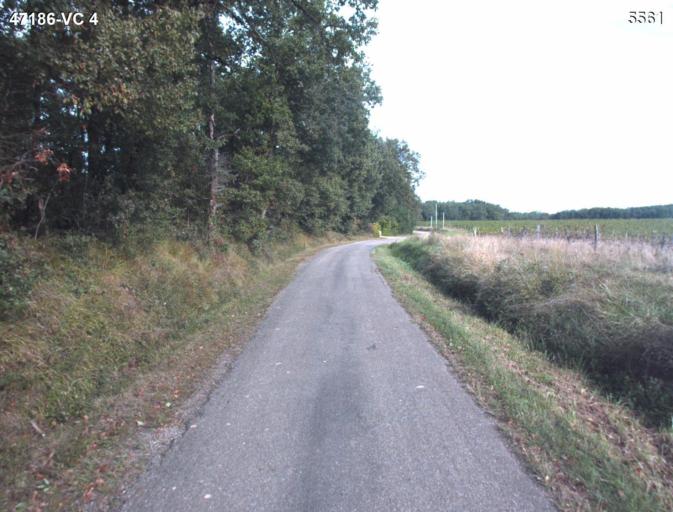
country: FR
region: Aquitaine
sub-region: Departement du Lot-et-Garonne
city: Sainte-Colombe-en-Bruilhois
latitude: 44.1862
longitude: 0.4592
